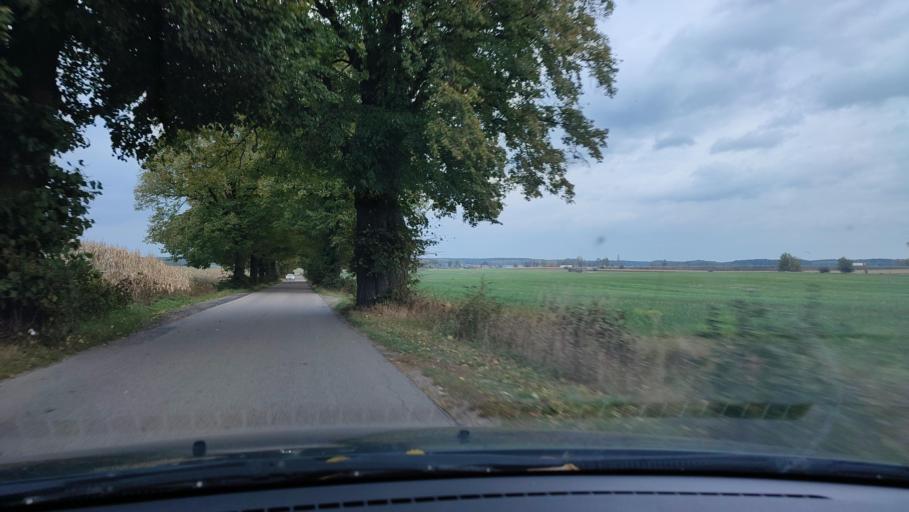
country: PL
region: Masovian Voivodeship
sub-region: Powiat mlawski
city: Wieczfnia Koscielna
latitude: 53.2200
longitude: 20.4097
